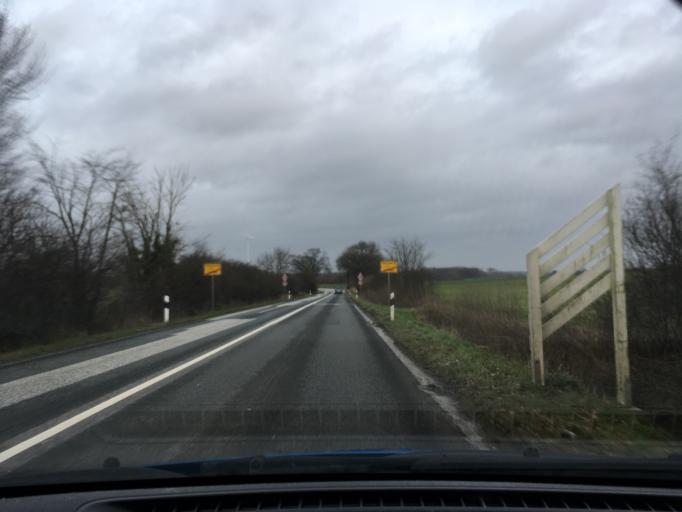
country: DE
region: Schleswig-Holstein
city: Lutau
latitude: 53.4393
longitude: 10.5556
